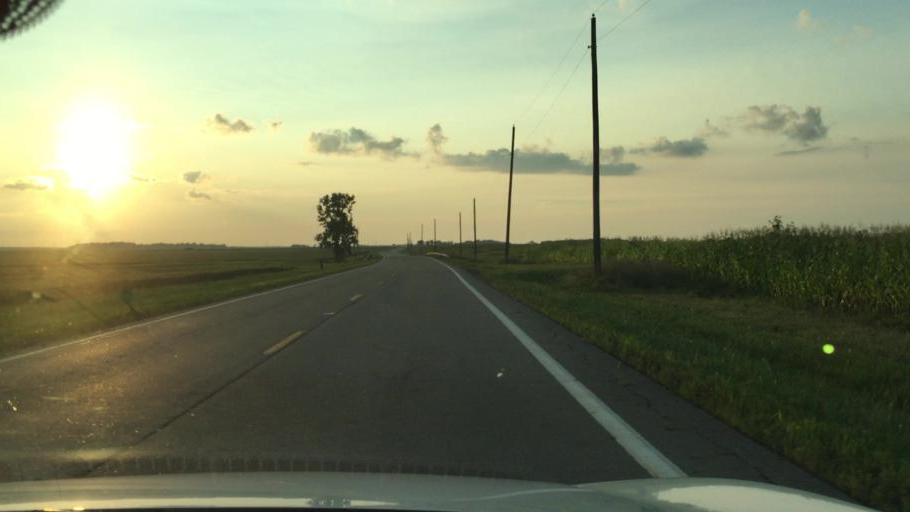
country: US
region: Ohio
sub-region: Madison County
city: Choctaw Lake
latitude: 40.0079
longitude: -83.4471
